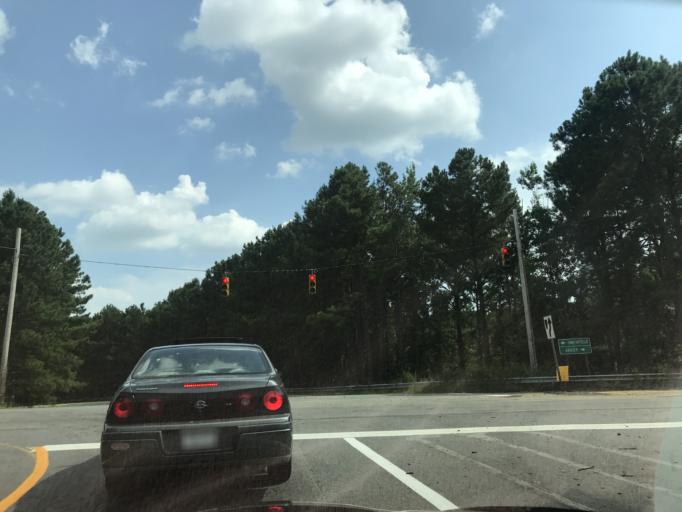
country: US
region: North Carolina
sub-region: Johnston County
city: Benson
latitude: 35.5166
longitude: -78.5589
